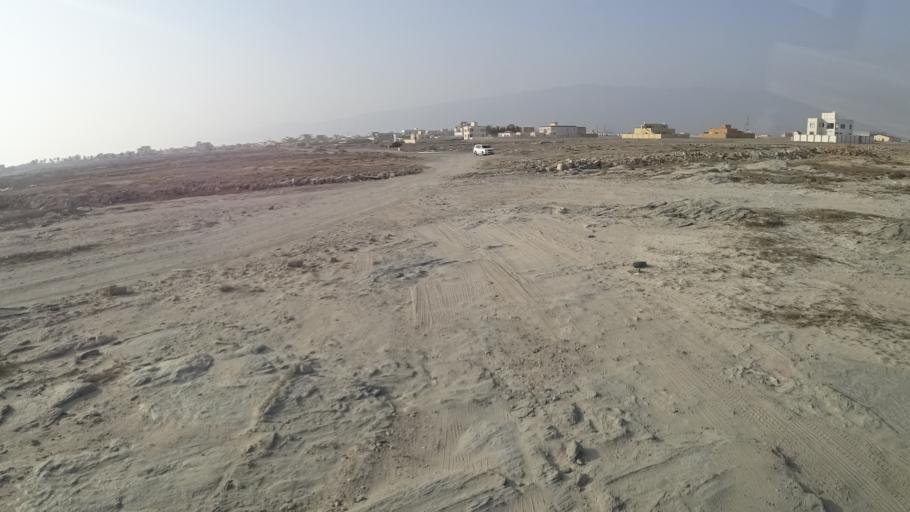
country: OM
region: Zufar
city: Salalah
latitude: 16.9740
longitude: 54.7005
